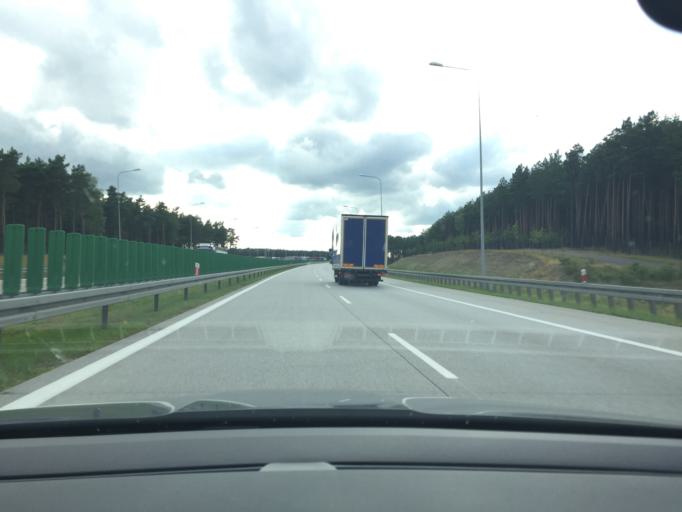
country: PL
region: Lubusz
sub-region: Powiat slubicki
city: Slubice
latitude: 52.3241
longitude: 14.6634
